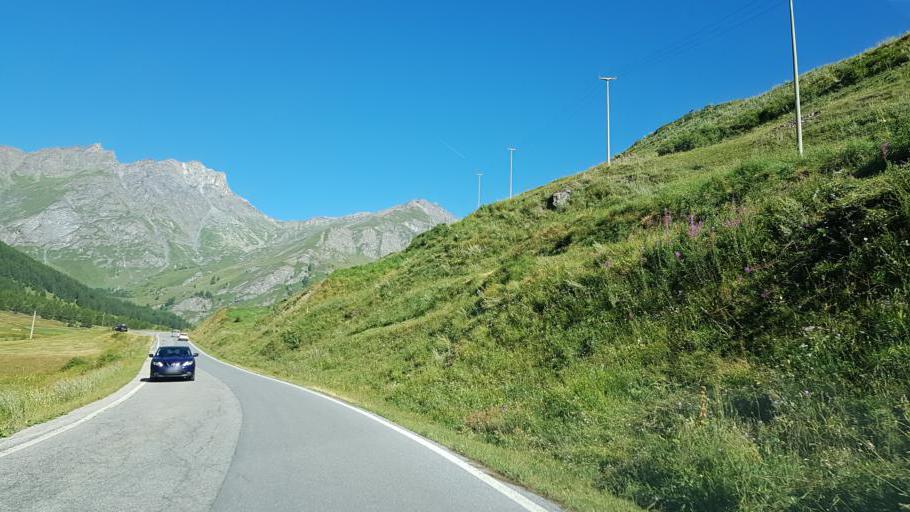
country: IT
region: Piedmont
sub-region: Provincia di Cuneo
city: Pontechianale
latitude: 44.6407
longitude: 7.0100
